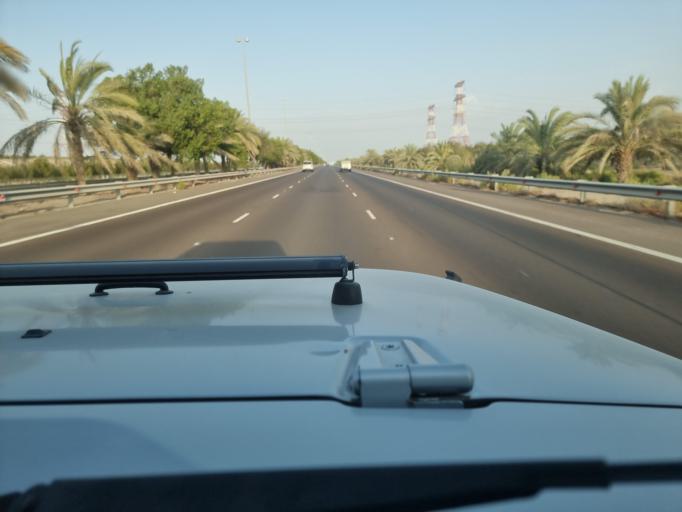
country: AE
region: Abu Dhabi
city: Abu Dhabi
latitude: 24.2280
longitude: 54.7881
